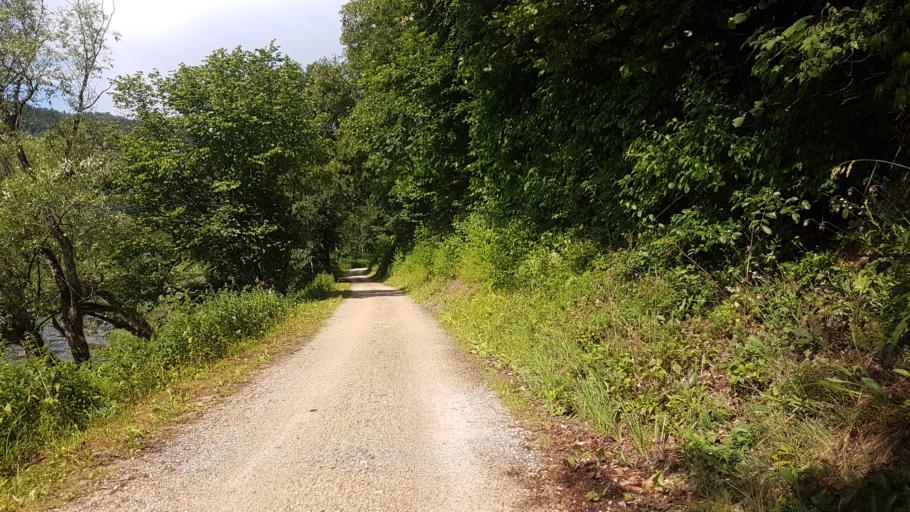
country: DE
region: Baden-Wuerttemberg
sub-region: Tuebingen Region
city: Leibertingen
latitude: 48.0729
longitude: 9.0241
